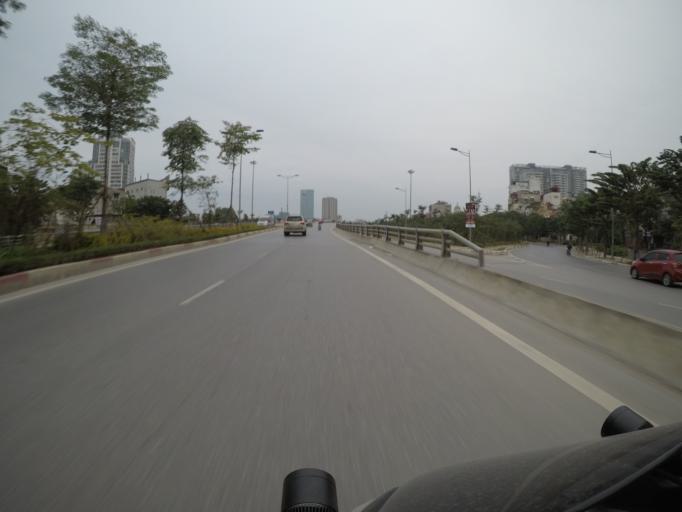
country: VN
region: Ha Noi
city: Cau Giay
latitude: 21.0482
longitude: 105.8050
